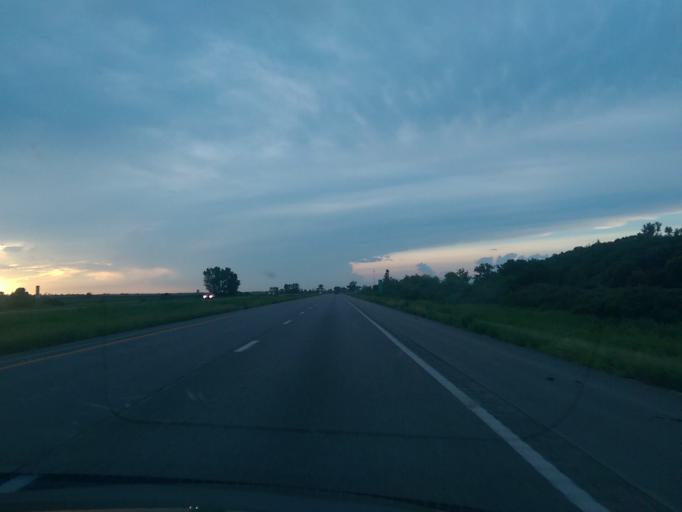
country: US
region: Missouri
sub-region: Atchison County
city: Rock Port
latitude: 40.2820
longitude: -95.4757
